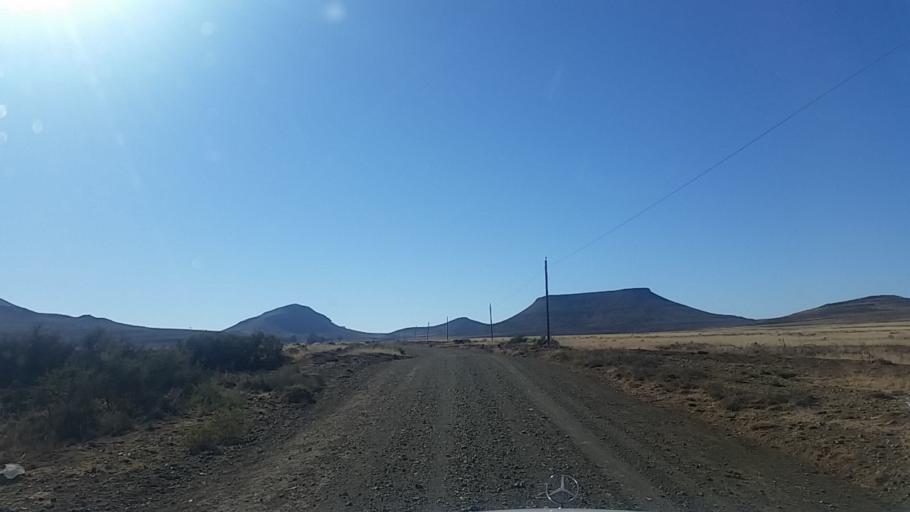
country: ZA
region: Eastern Cape
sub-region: Chris Hani District Municipality
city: Middelburg
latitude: -31.7957
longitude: 24.7049
